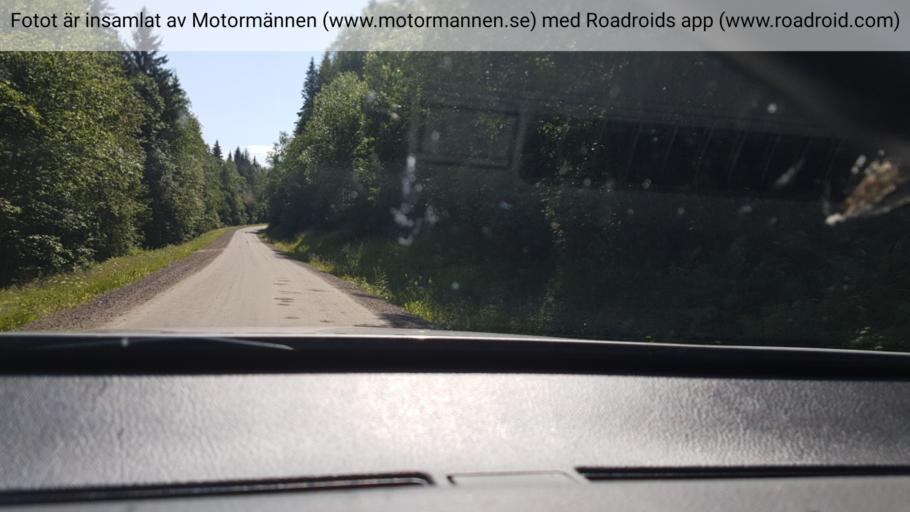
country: SE
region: Vaermland
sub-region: Torsby Kommun
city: Torsby
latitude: 60.5987
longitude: 13.0467
